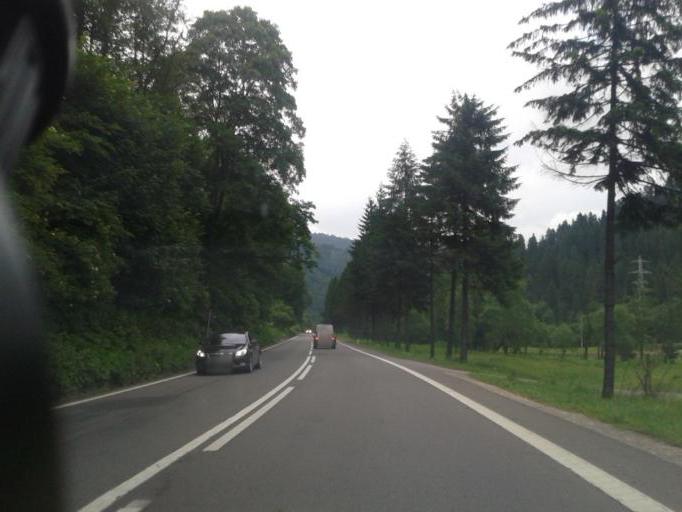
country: RO
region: Brasov
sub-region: Oras Predeal
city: Predeal
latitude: 45.5431
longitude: 25.5887
